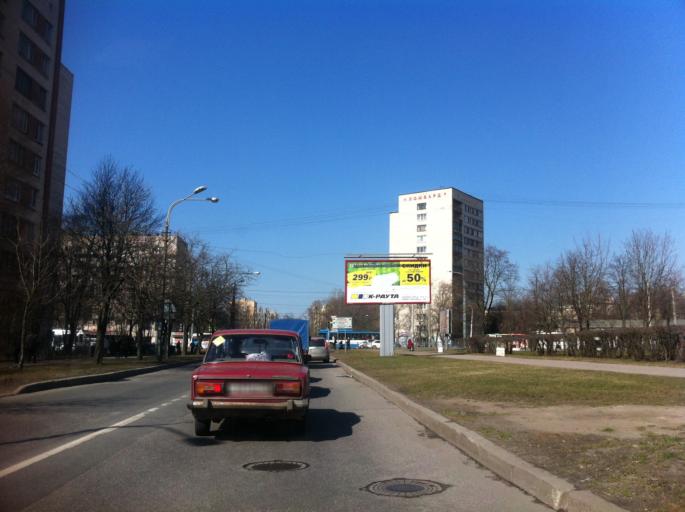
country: RU
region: St.-Petersburg
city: Dachnoye
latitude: 59.8415
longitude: 30.2456
